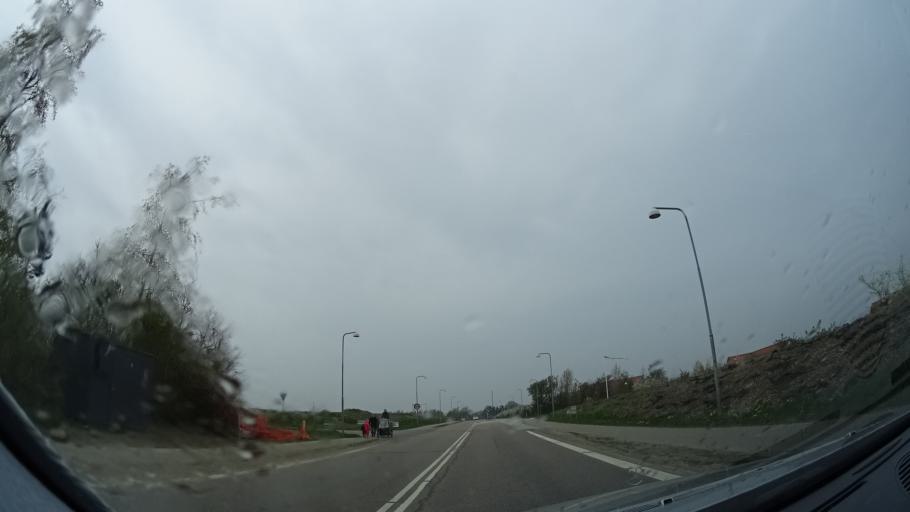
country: DK
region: Zealand
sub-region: Holbaek Kommune
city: Vipperod
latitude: 55.7071
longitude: 11.7634
